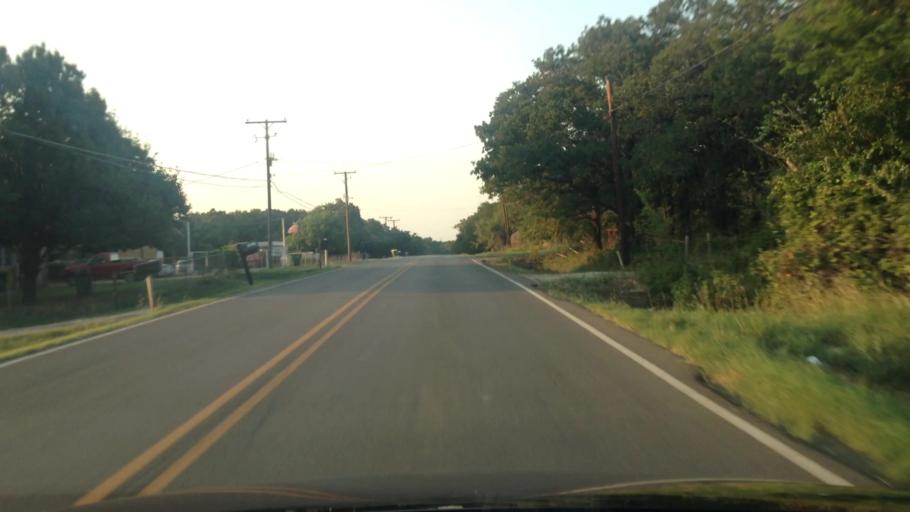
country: US
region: Texas
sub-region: Tarrant County
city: Rendon
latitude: 32.6027
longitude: -97.2154
